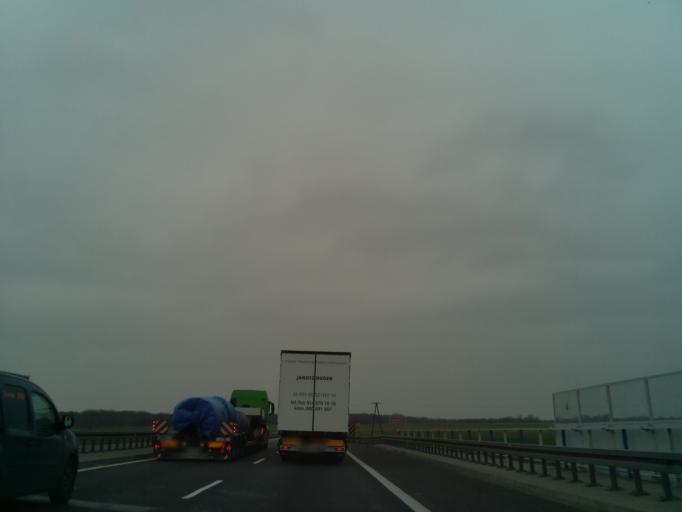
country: PL
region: Lower Silesian Voivodeship
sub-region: Powiat wroclawski
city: Katy Wroclawskie
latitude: 51.0193
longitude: 16.7048
